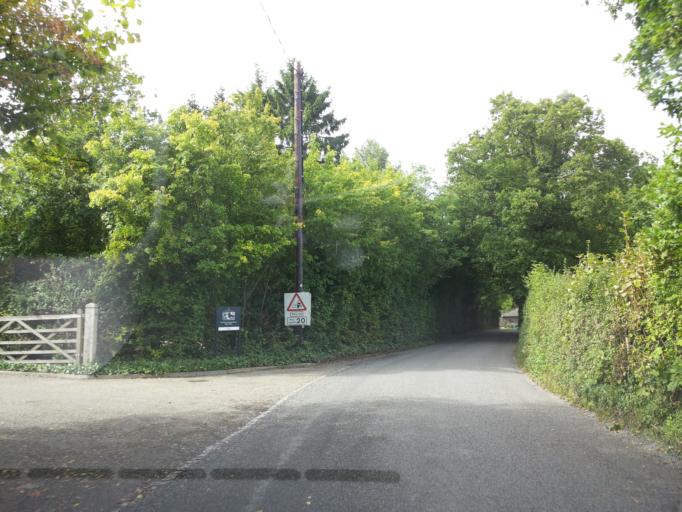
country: GB
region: England
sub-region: Kent
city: Biggin Hill
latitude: 51.3319
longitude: 0.0526
